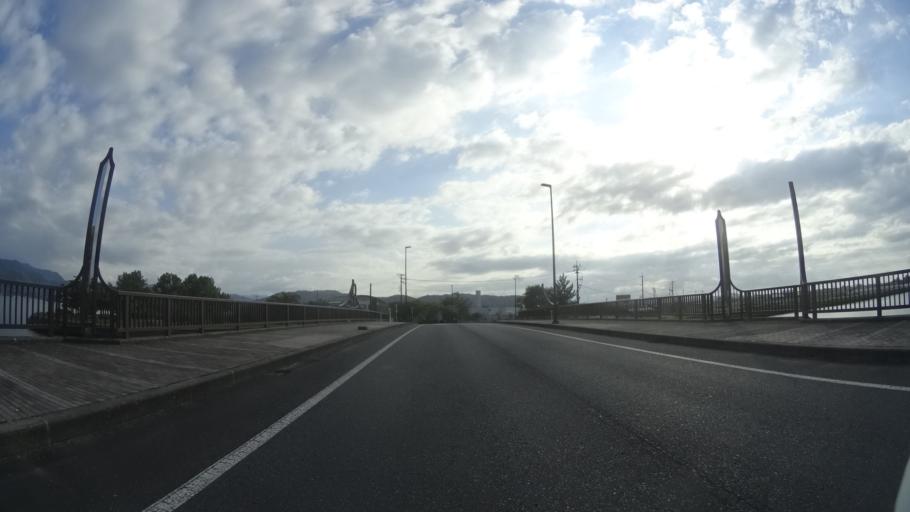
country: JP
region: Tottori
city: Kurayoshi
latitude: 35.4917
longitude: 133.8844
